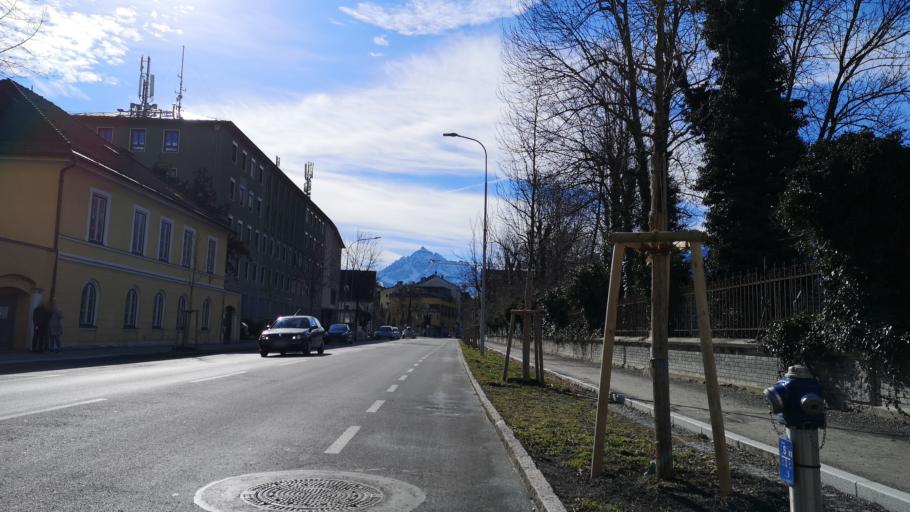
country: AT
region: Tyrol
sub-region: Innsbruck Stadt
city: Innsbruck
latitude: 47.2716
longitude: 11.4001
